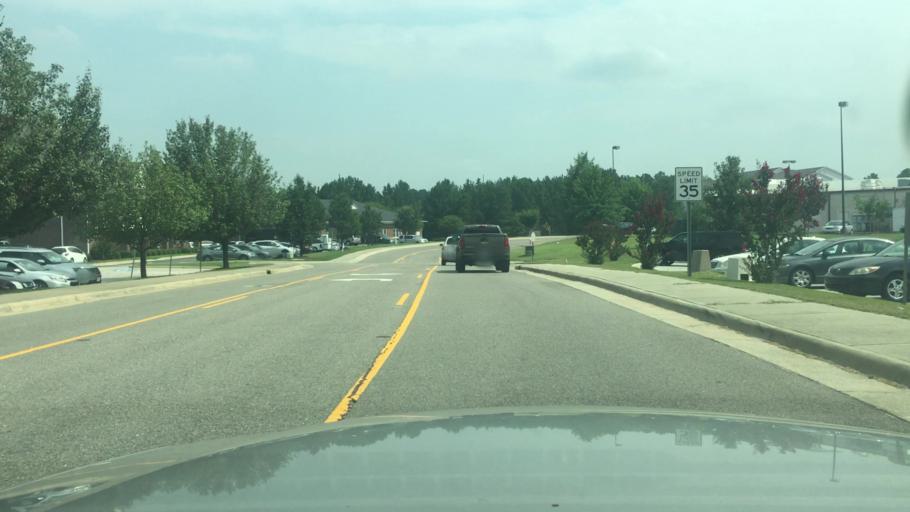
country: US
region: North Carolina
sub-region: Cumberland County
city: Fayetteville
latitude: 35.0379
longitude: -78.9382
